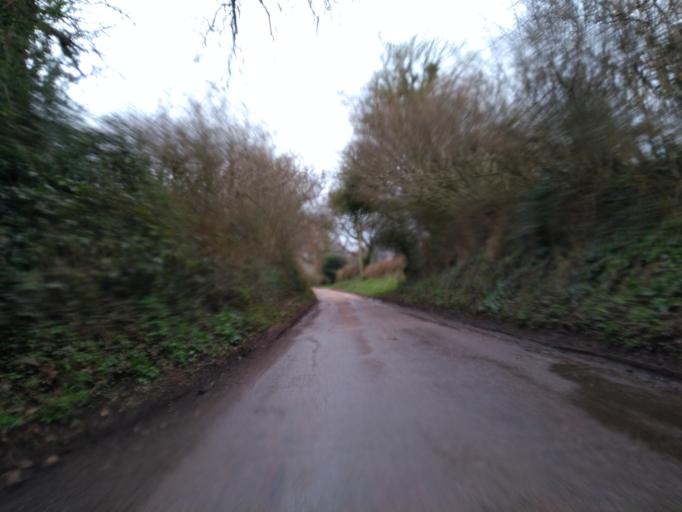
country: GB
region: England
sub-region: Devon
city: Heavitree
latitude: 50.8003
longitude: -3.4901
